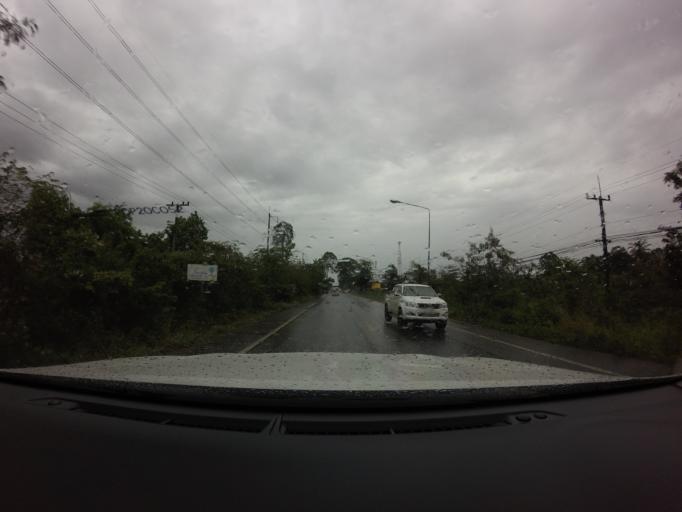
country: TH
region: Chachoengsao
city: Phanom Sarakham
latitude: 13.7924
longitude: 101.4007
